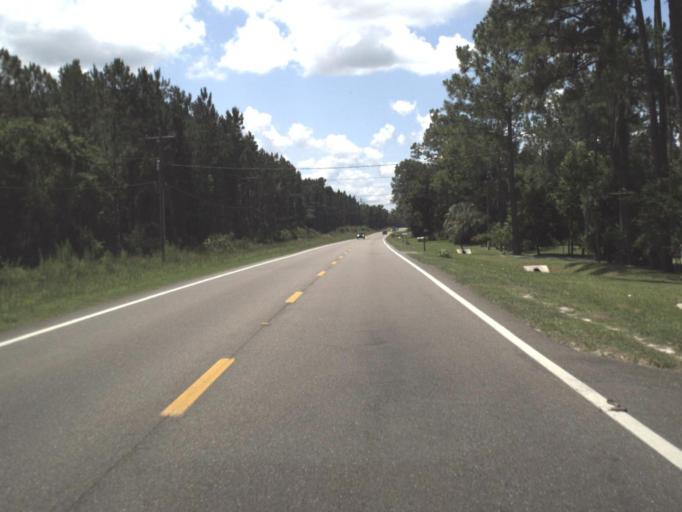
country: US
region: Florida
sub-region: Clay County
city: Keystone Heights
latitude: 29.7388
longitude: -82.0505
